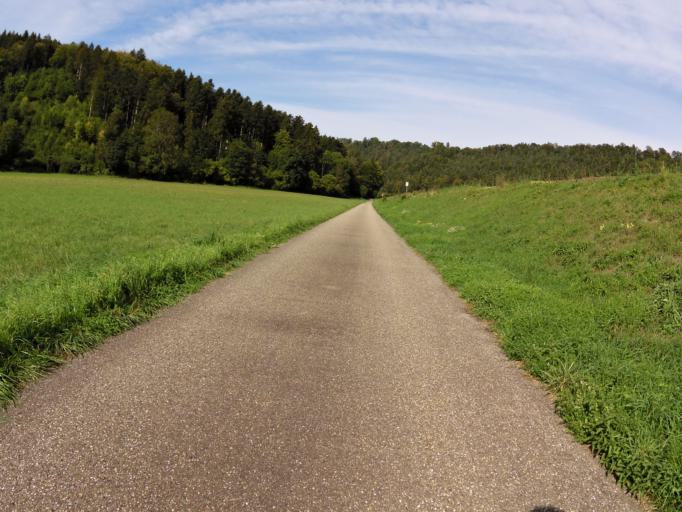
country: DE
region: Baden-Wuerttemberg
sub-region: Karlsruhe Region
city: Horb am Neckar
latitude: 48.4517
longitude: 8.7541
